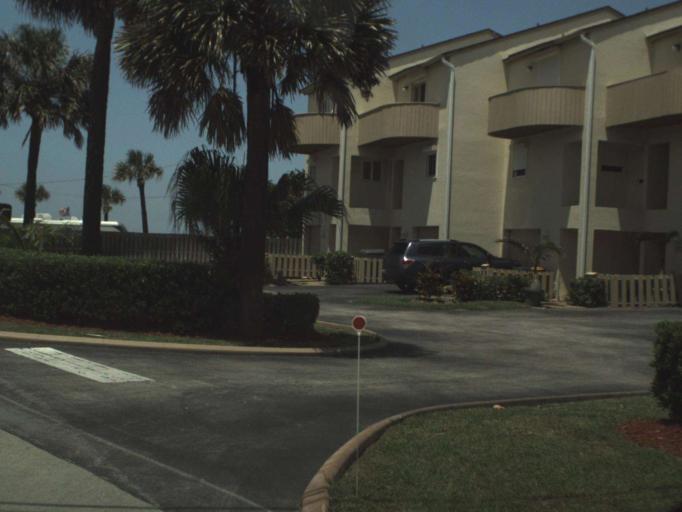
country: US
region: Florida
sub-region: Brevard County
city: Melbourne Beach
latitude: 28.0436
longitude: -80.5461
